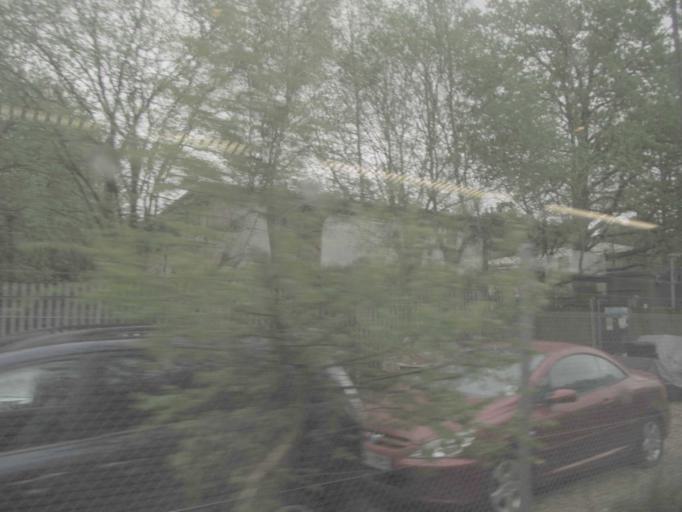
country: GB
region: England
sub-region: Hampshire
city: Yateley
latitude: 51.3657
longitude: -0.8187
